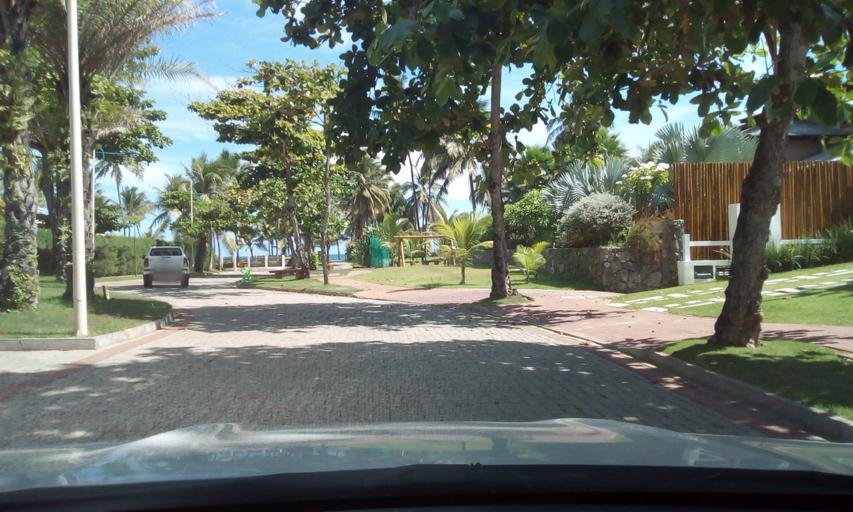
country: BR
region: Bahia
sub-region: Lauro De Freitas
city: Lauro de Freitas
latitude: -12.8733
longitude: -38.2721
